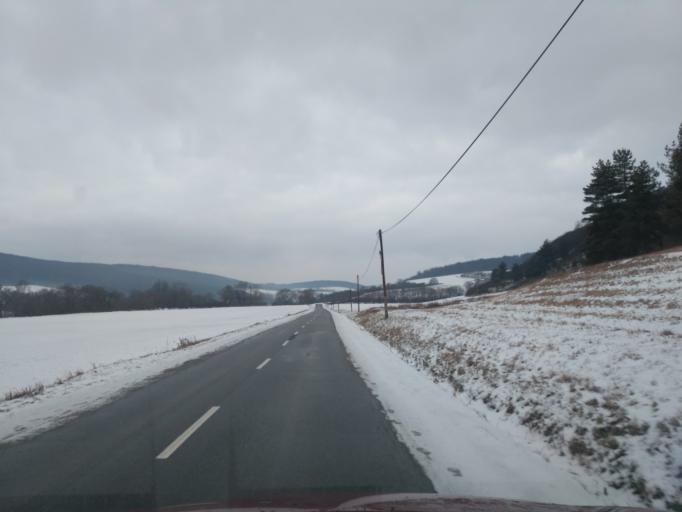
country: SK
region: Presovsky
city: Sabinov
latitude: 49.0179
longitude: 21.1160
